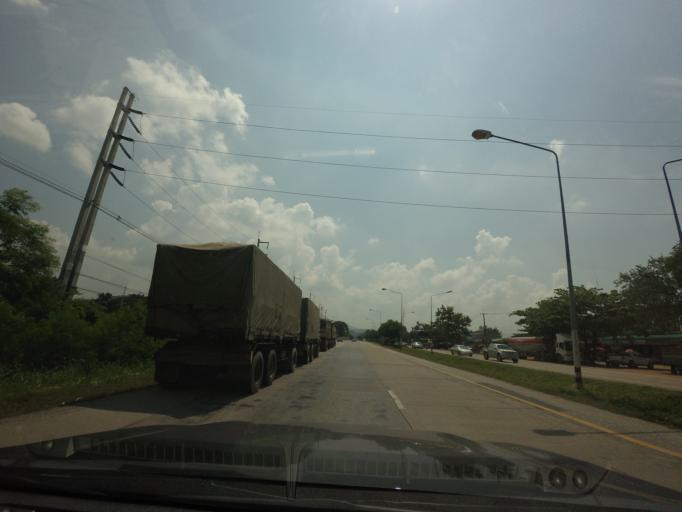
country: TH
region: Uttaradit
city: Thong Saen Khan
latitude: 17.4734
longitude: 100.2361
